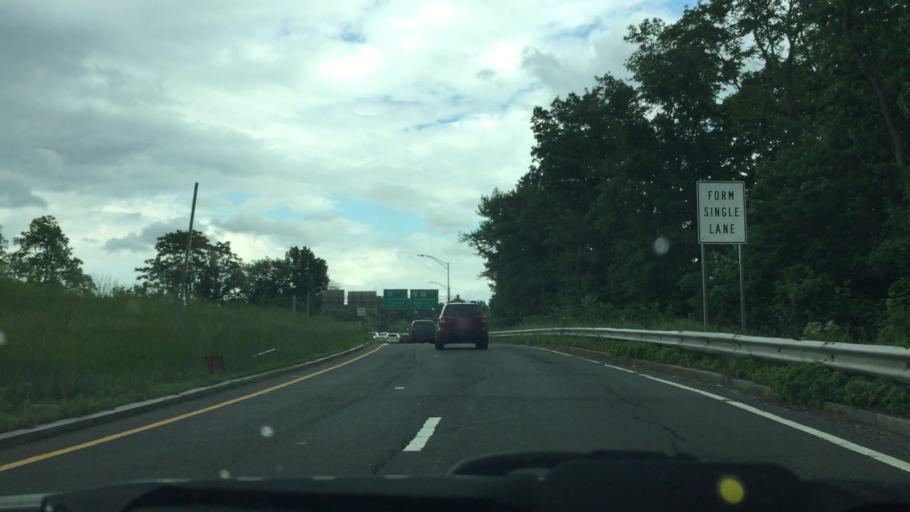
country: US
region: Massachusetts
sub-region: Hampden County
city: Springfield
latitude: 42.0804
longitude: -72.5876
